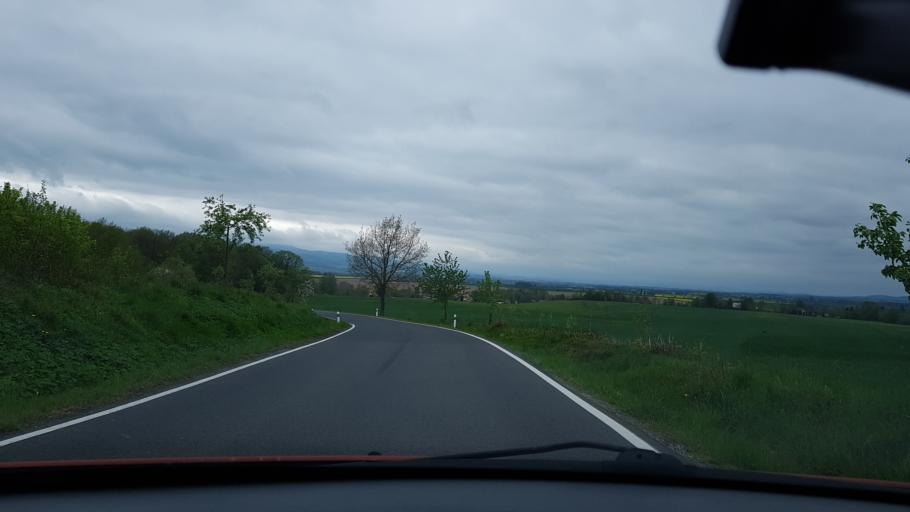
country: CZ
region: Olomoucky
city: Vidnava
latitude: 50.3866
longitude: 17.1339
